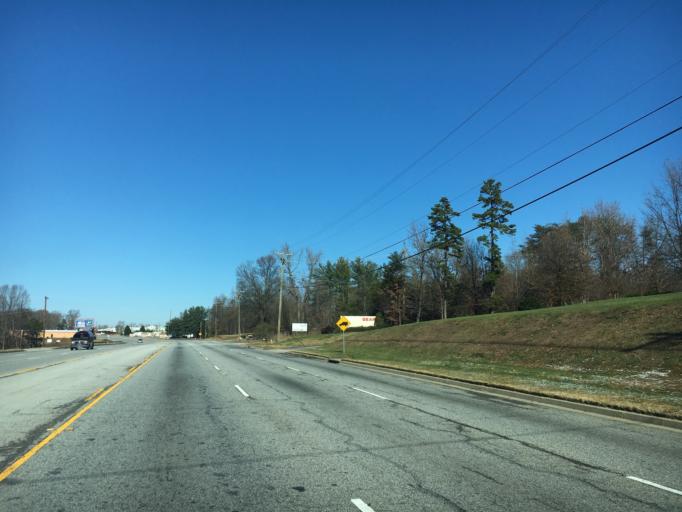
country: US
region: South Carolina
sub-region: Greenville County
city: Greer
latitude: 34.8974
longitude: -82.2352
